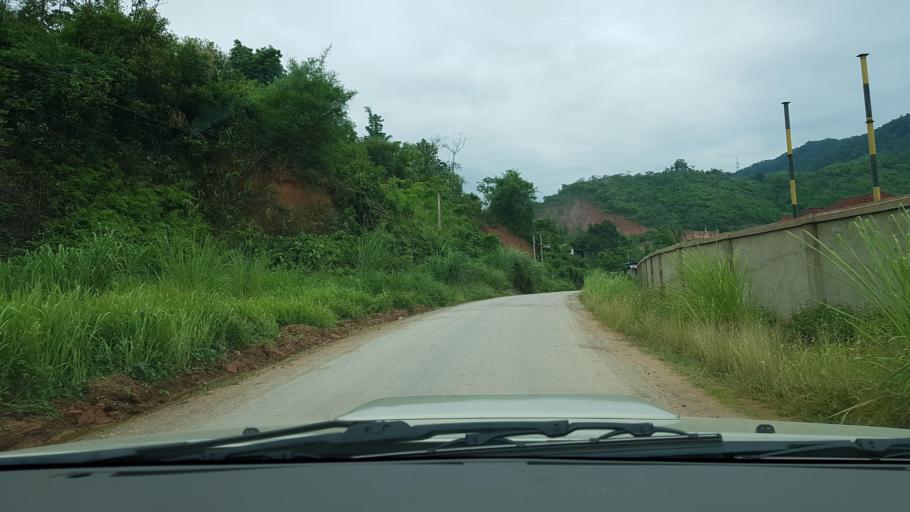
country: LA
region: Oudomxai
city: Muang Xay
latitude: 20.6544
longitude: 101.9787
